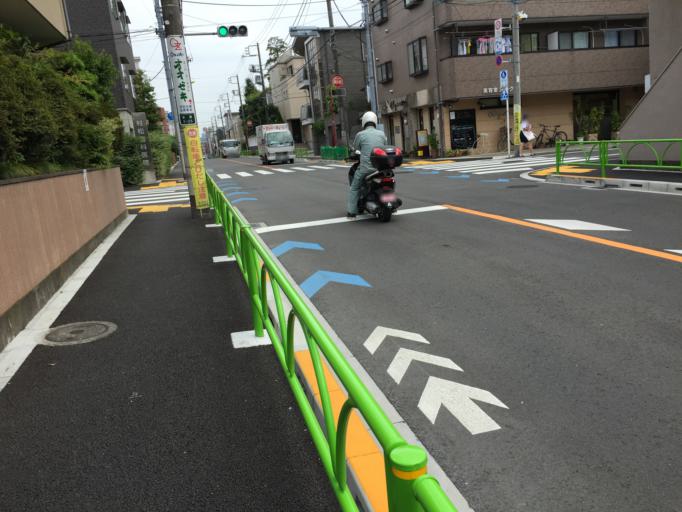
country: JP
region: Tokyo
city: Tokyo
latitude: 35.6570
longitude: 139.6391
